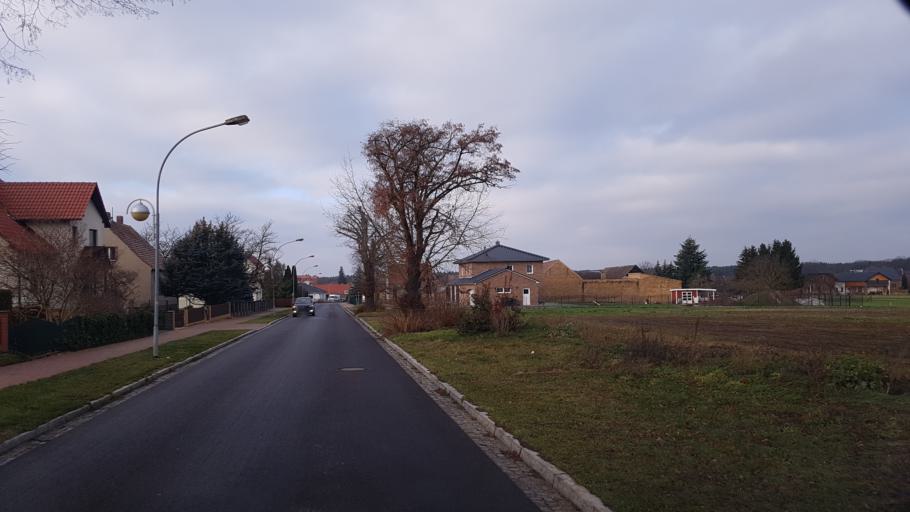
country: DE
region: Brandenburg
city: Sallgast
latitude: 51.5952
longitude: 13.7836
